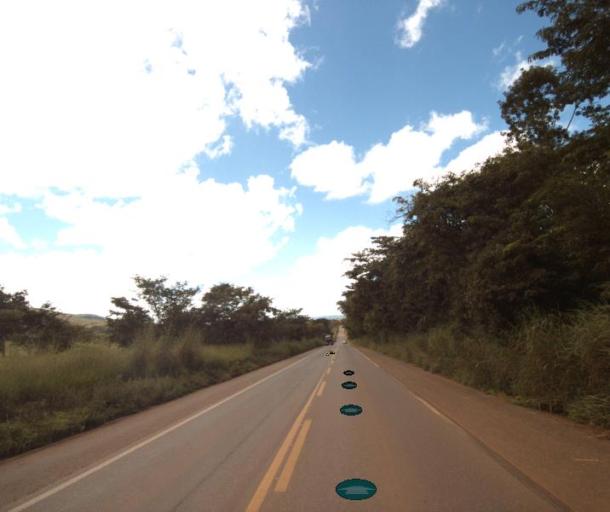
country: BR
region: Goias
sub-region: Petrolina De Goias
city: Petrolina de Goias
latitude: -15.9846
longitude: -49.1575
